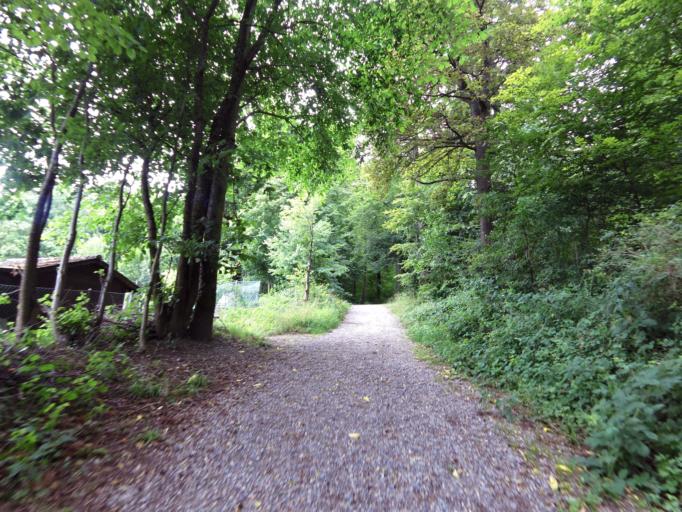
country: CH
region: Zurich
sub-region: Bezirk Zuerich
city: Zuerich (Kreis 10) / Wipkingen
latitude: 47.4006
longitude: 8.5243
